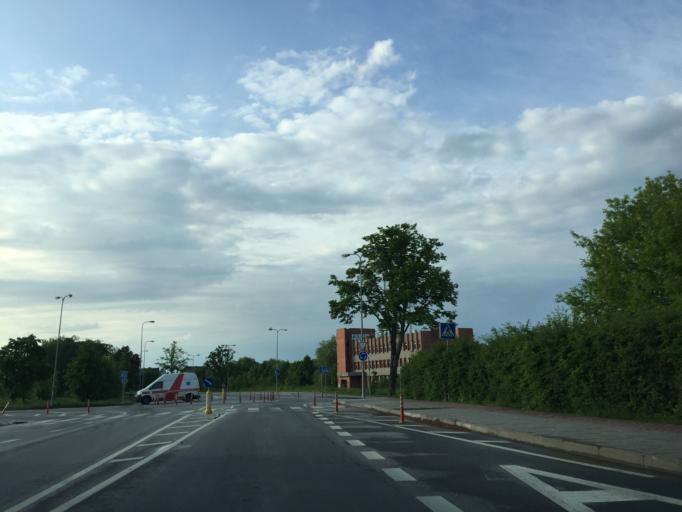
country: LT
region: Klaipedos apskritis
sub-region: Klaipeda
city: Klaipeda
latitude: 55.7526
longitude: 21.1331
